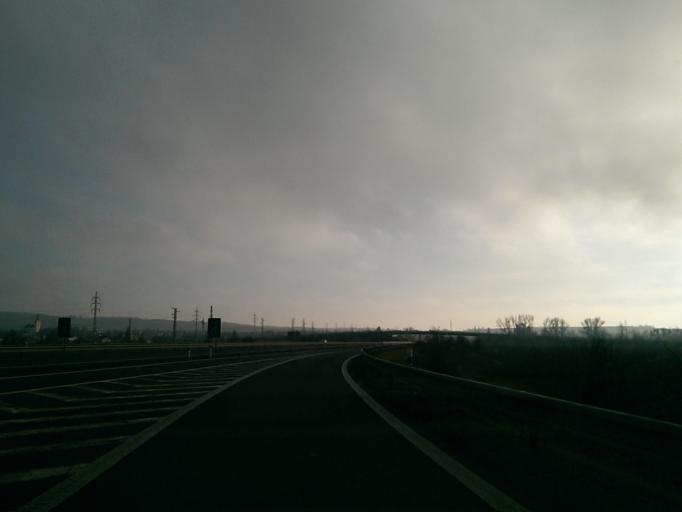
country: CZ
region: Olomoucky
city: Velky Tynec
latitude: 49.5566
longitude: 17.3173
